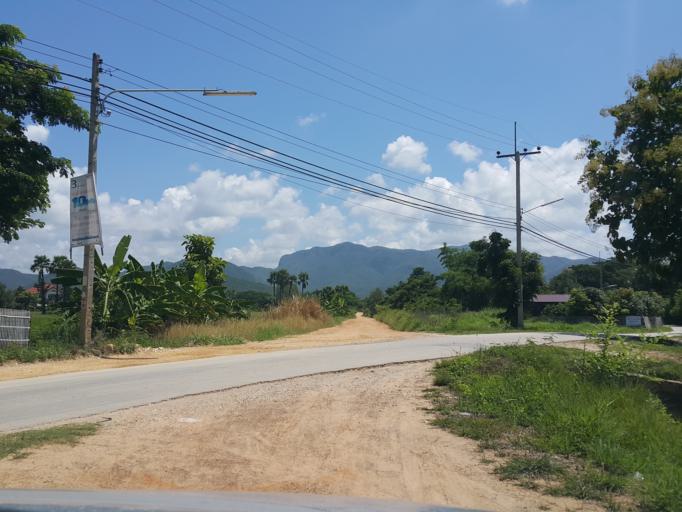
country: TH
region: Lamphun
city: Ban Thi
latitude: 18.6693
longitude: 99.1483
